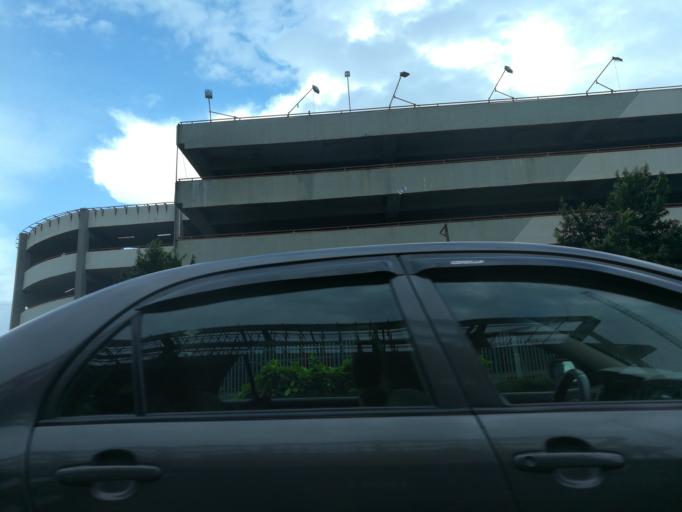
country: NG
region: Lagos
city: Ikeja
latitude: 6.5838
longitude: 3.3339
